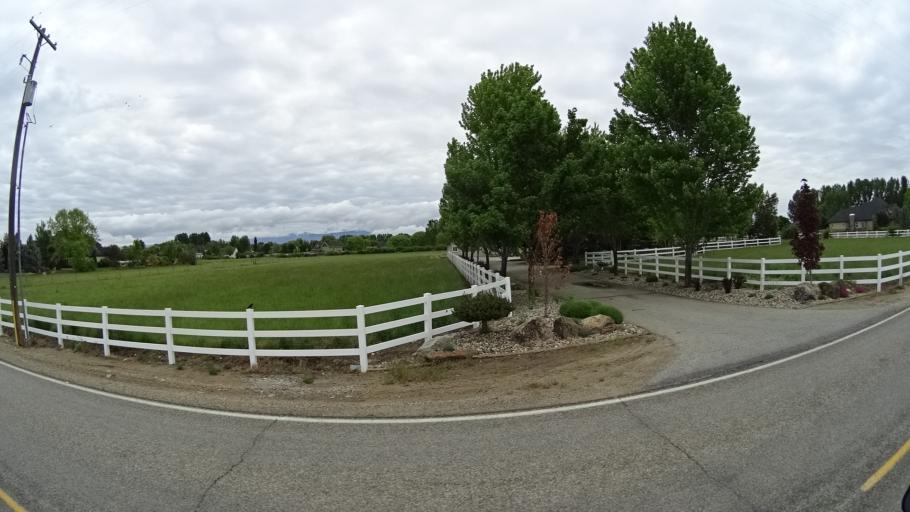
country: US
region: Idaho
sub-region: Ada County
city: Eagle
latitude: 43.7180
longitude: -116.4136
